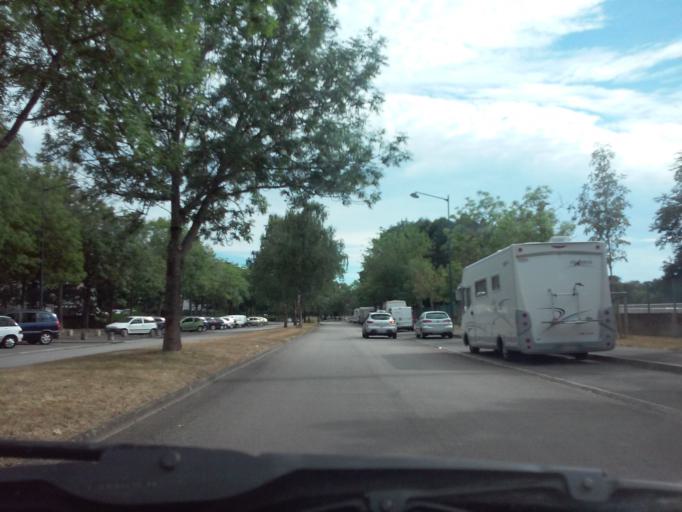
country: FR
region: Brittany
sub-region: Departement d'Ille-et-Vilaine
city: Rennes
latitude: 48.0893
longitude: -1.6854
